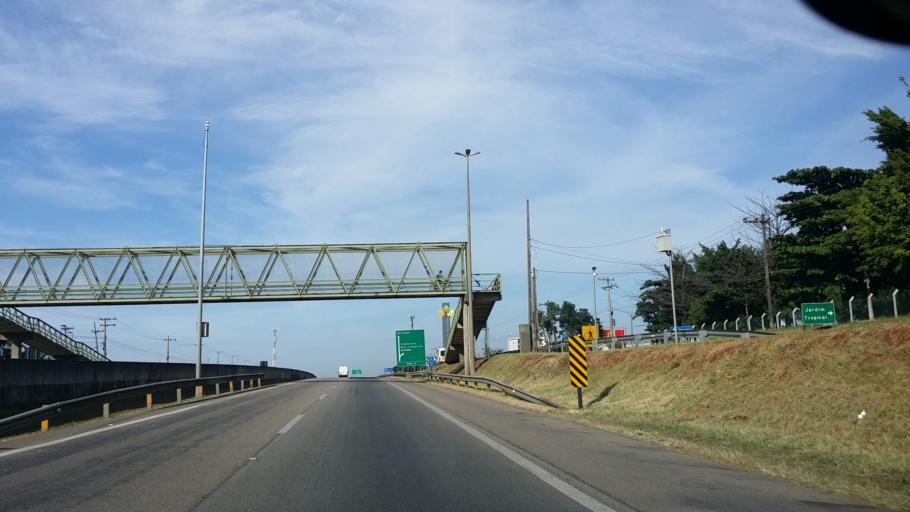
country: BR
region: Sao Paulo
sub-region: Indaiatuba
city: Indaiatuba
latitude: -23.1166
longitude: -47.2165
